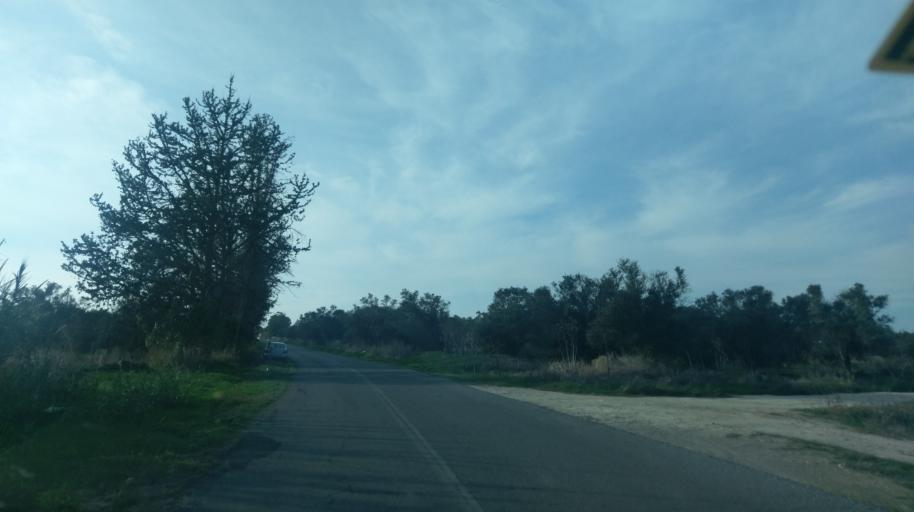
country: CY
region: Ammochostos
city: Achna
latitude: 35.1069
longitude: 33.7591
